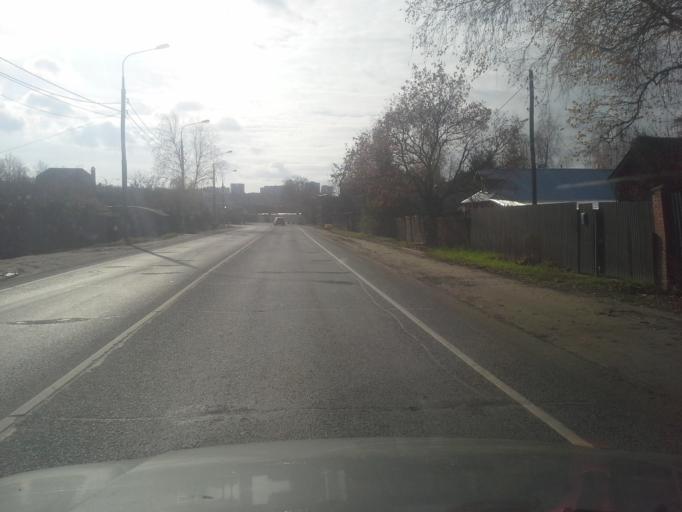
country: RU
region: Moskovskaya
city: Zvenigorod
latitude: 55.7162
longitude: 36.8664
